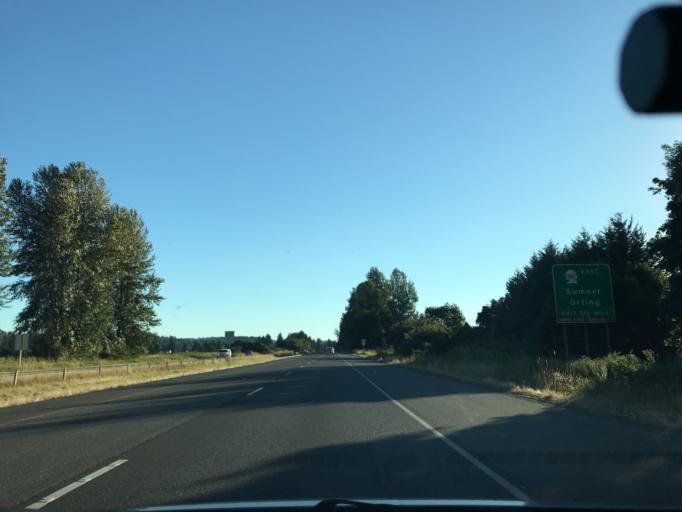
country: US
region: Washington
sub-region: Pierce County
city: Sumner
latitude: 47.1963
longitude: -122.2160
